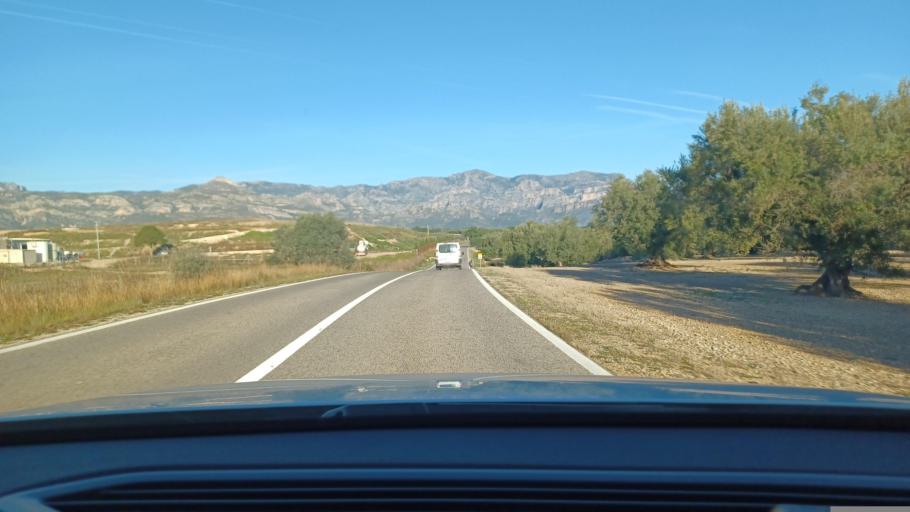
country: ES
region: Catalonia
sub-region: Provincia de Tarragona
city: Mas de Barberans
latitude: 40.7130
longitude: 0.4045
